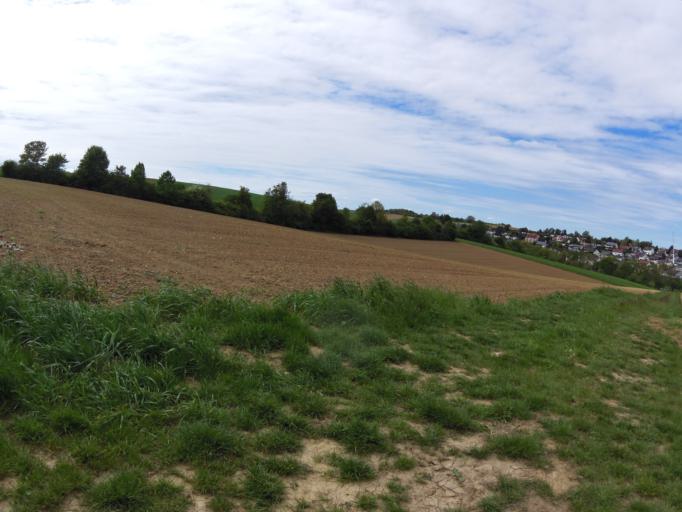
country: DE
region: Bavaria
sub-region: Regierungsbezirk Unterfranken
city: Kurnach
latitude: 49.8400
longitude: 10.0341
